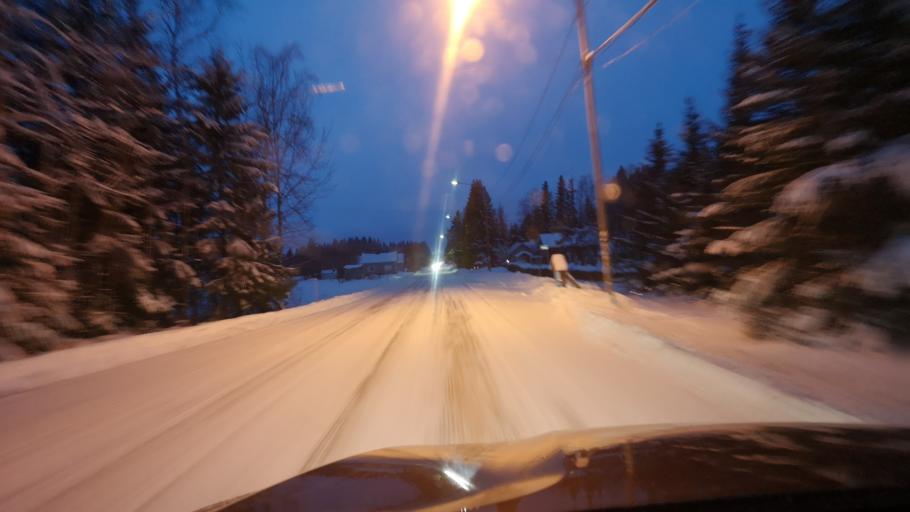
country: FI
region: Varsinais-Suomi
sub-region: Loimaa
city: Loimaa
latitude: 60.8717
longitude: 23.0901
